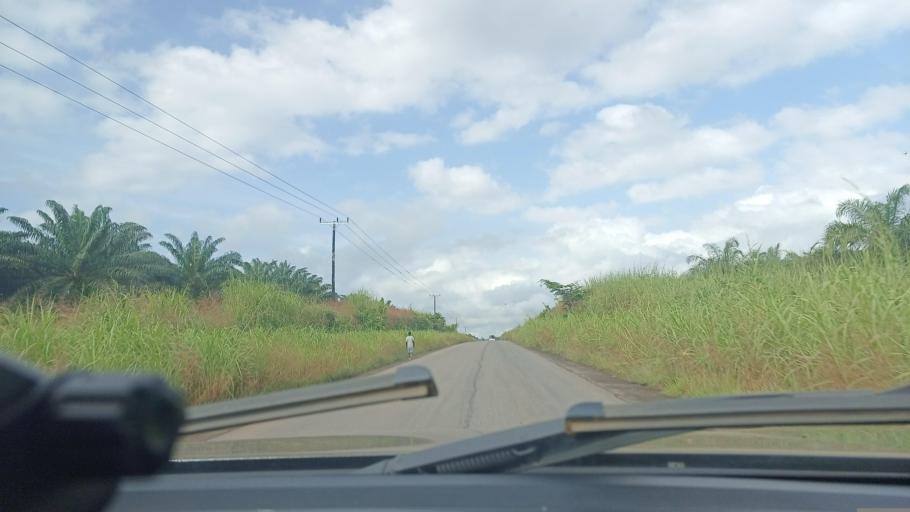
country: LR
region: Bomi
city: Tubmanburg
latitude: 6.7284
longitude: -11.0285
